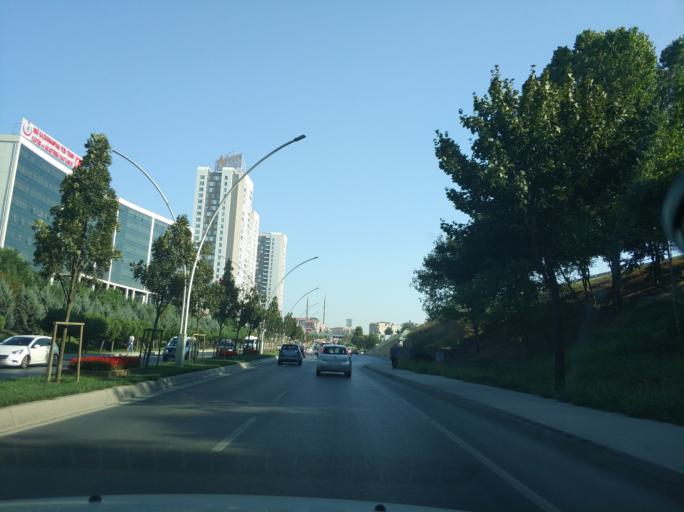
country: TR
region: Istanbul
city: Sultangazi
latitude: 41.0905
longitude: 28.9066
